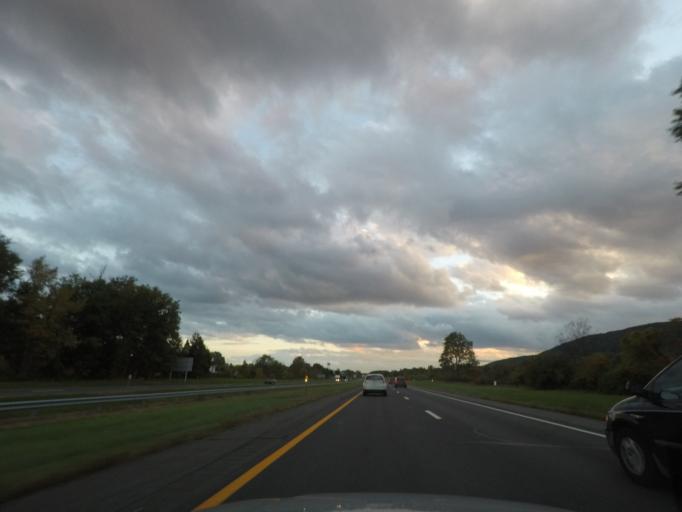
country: US
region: New York
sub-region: Ulster County
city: Saugerties
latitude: 42.0696
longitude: -73.9775
